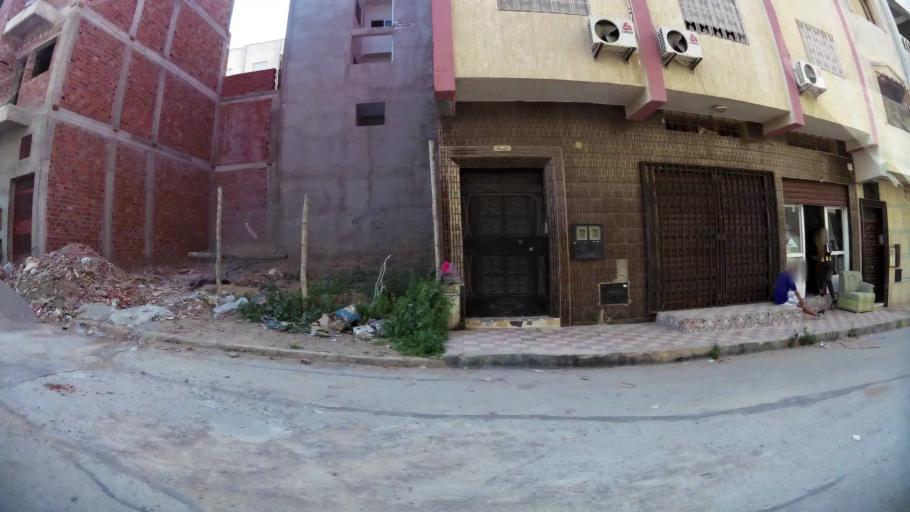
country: MA
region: Tanger-Tetouan
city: Tetouan
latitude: 35.5890
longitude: -5.3496
